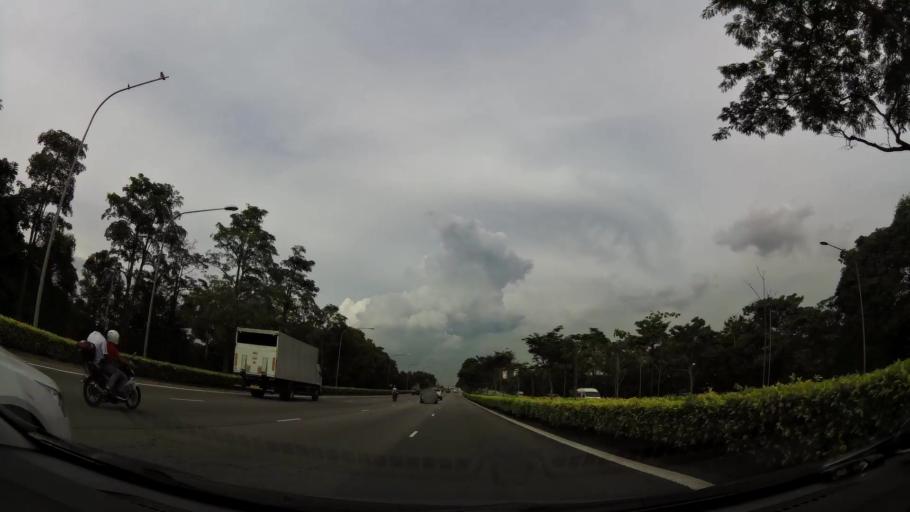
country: MY
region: Johor
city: Johor Bahru
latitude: 1.3771
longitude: 103.7303
